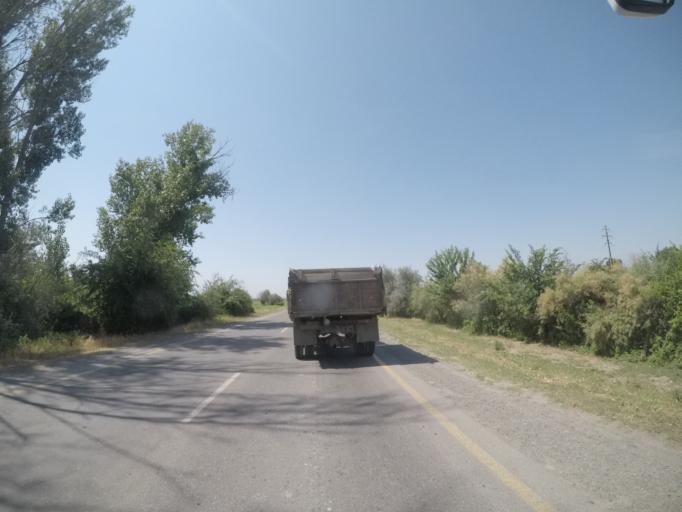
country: AZ
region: Agdas
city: Agdas
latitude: 40.5877
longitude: 47.4431
